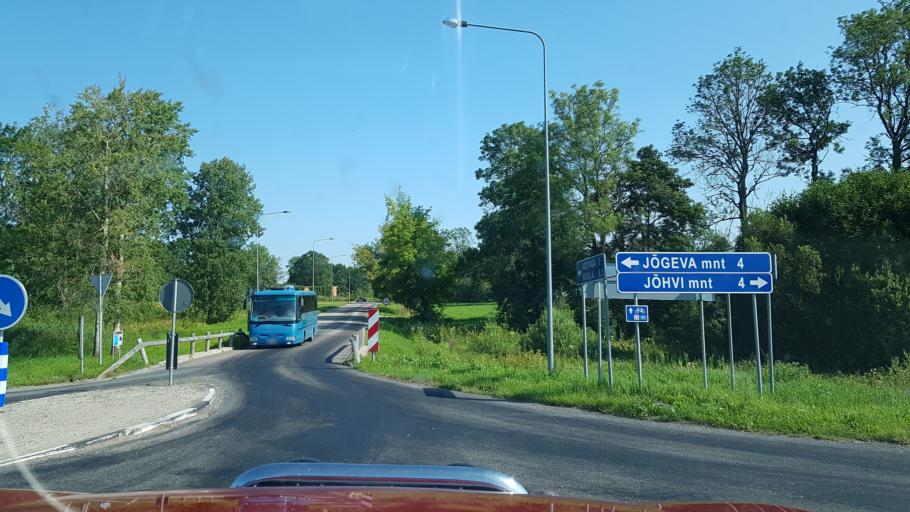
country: EE
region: Tartu
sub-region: Tartu linn
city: Tartu
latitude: 58.4685
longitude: 26.7274
